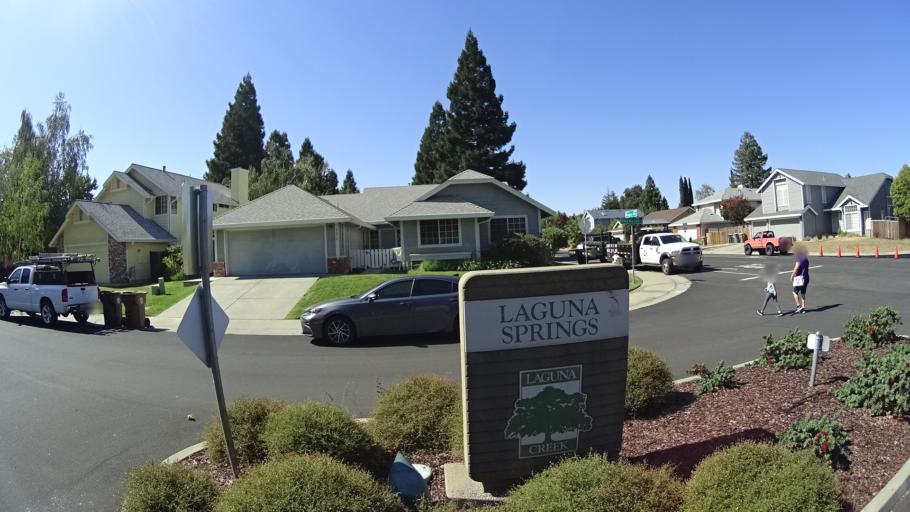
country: US
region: California
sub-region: Sacramento County
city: Laguna
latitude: 38.4279
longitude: -121.4364
